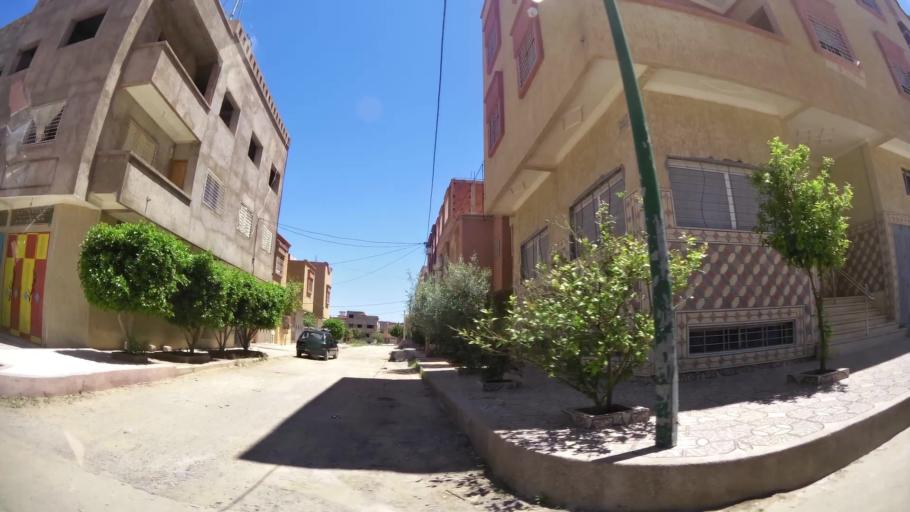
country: MA
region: Oriental
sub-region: Oujda-Angad
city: Oujda
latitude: 34.6669
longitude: -1.8822
